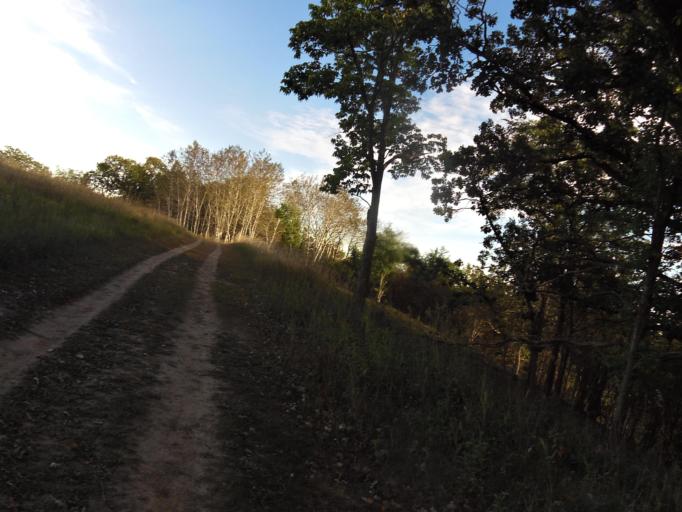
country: US
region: Minnesota
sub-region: Washington County
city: Afton
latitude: 44.8596
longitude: -92.7901
